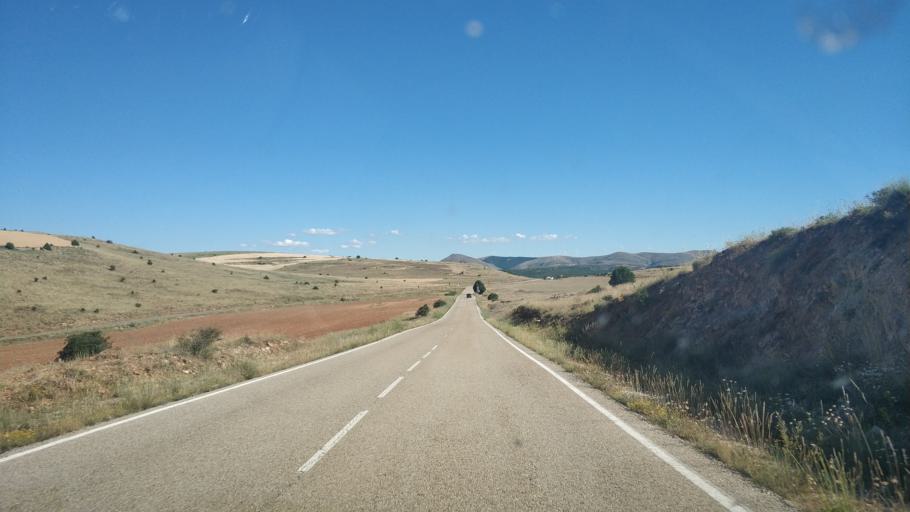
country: ES
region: Castille and Leon
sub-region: Provincia de Soria
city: Montejo de Tiermes
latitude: 41.3782
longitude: -3.1926
